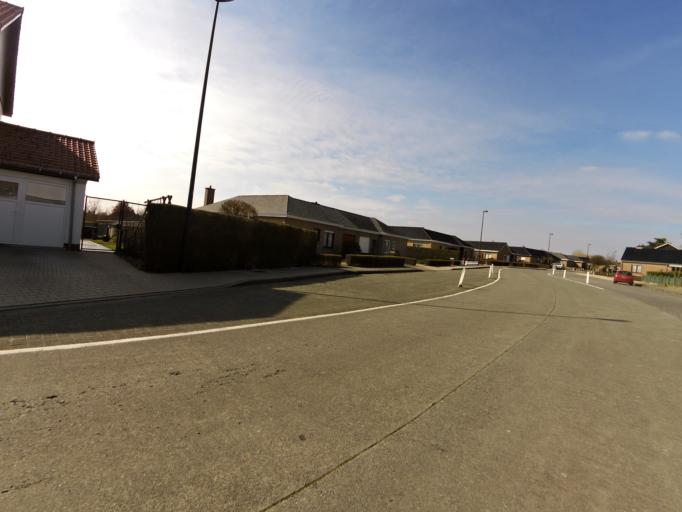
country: BE
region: Flanders
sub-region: Provincie West-Vlaanderen
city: Torhout
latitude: 51.0685
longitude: 3.0806
